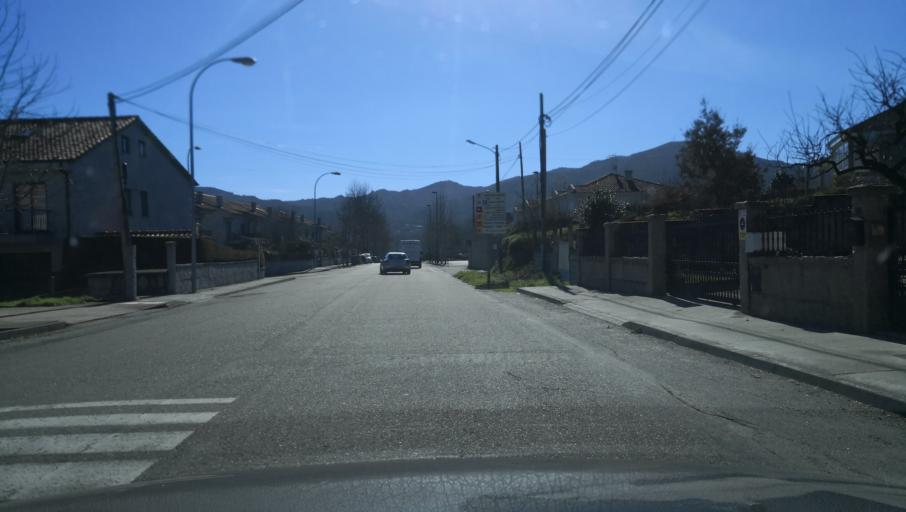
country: ES
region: Galicia
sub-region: Provincia de Ourense
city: Allariz
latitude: 42.1948
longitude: -7.8073
